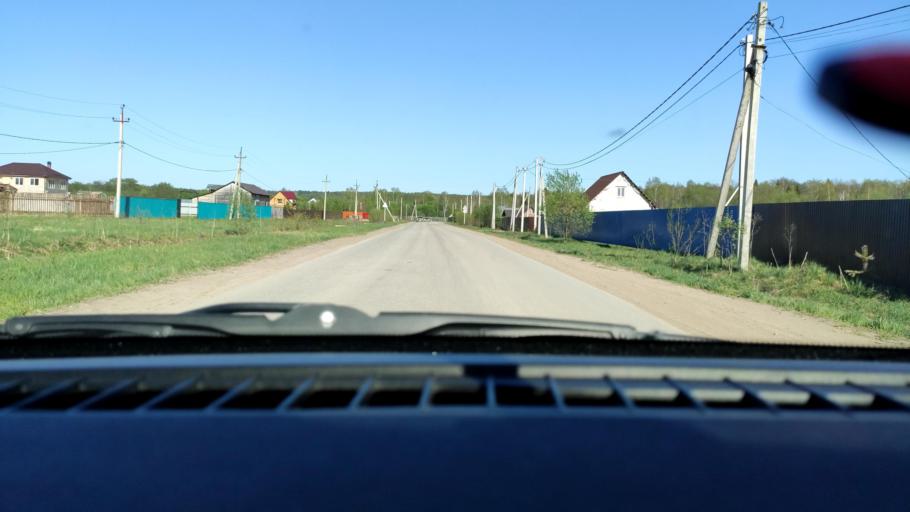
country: RU
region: Perm
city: Overyata
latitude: 58.0776
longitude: 55.9805
